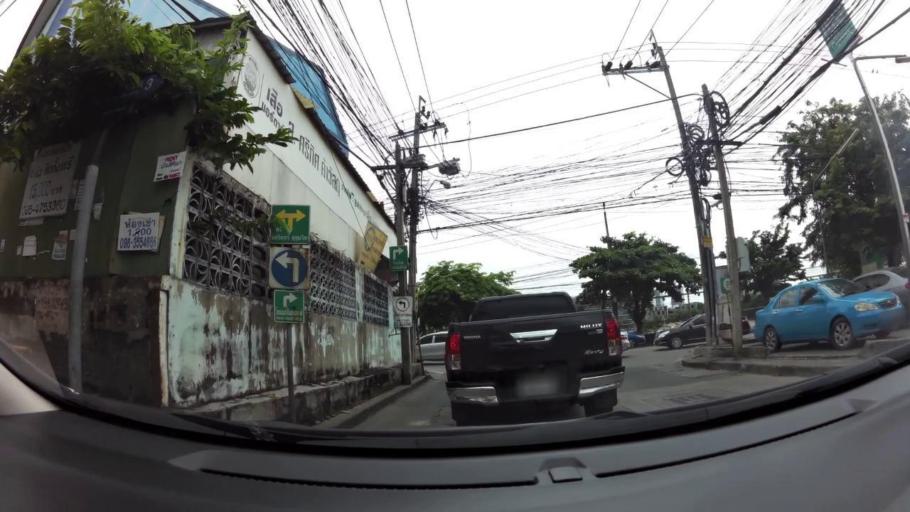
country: TH
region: Bangkok
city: Bang Na
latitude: 13.6781
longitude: 100.6376
